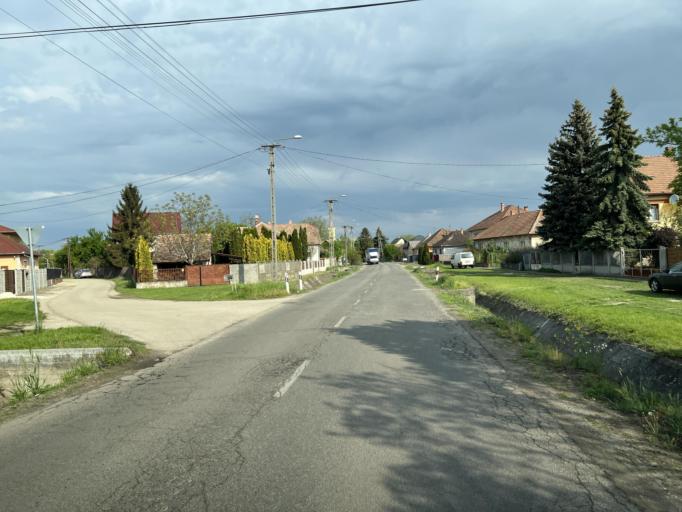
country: HU
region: Pest
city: Tapioszentmarton
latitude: 47.3380
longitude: 19.7507
